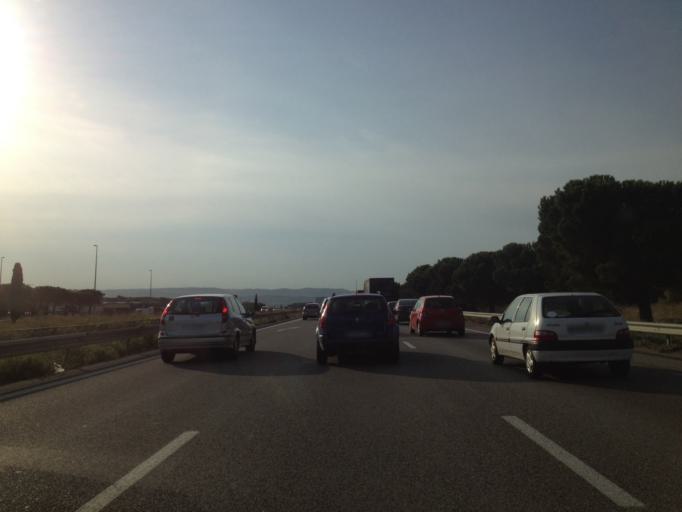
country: FR
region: Provence-Alpes-Cote d'Azur
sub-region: Departement des Bouches-du-Rhone
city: Vitrolles
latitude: 43.4478
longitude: 5.2408
